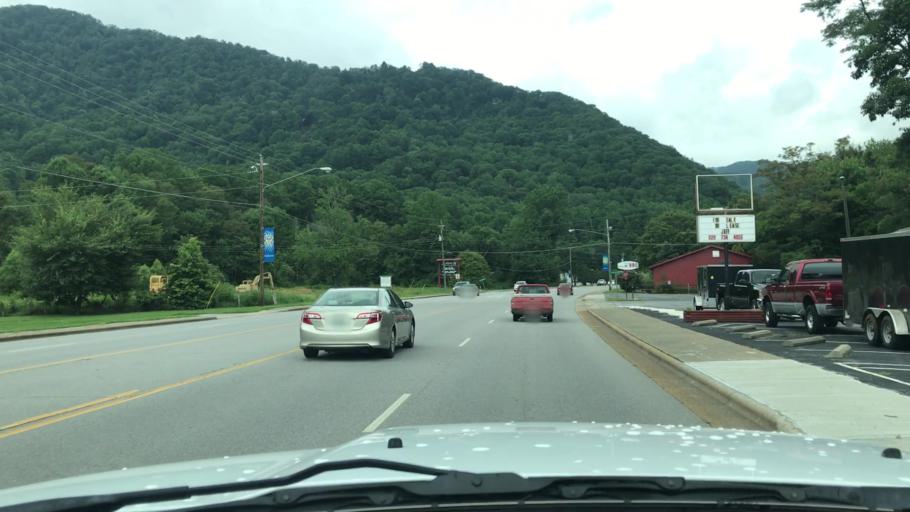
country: US
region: North Carolina
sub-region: Haywood County
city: Maggie Valley
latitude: 35.5182
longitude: -83.1010
